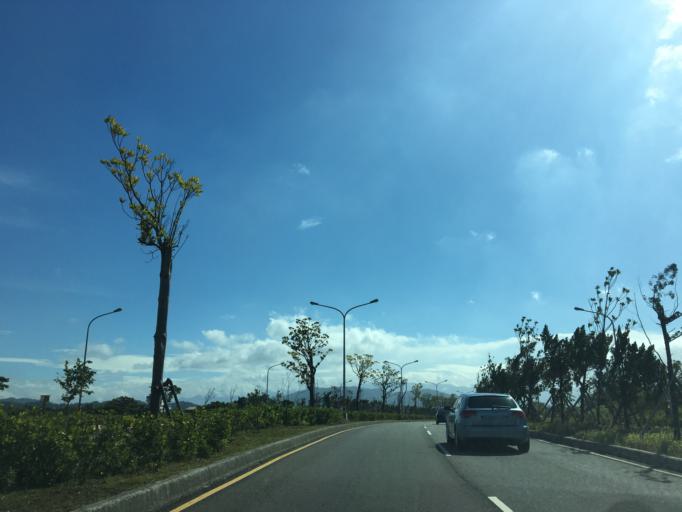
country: TW
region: Taiwan
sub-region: Hsinchu
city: Zhubei
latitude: 24.7815
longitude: 121.0503
